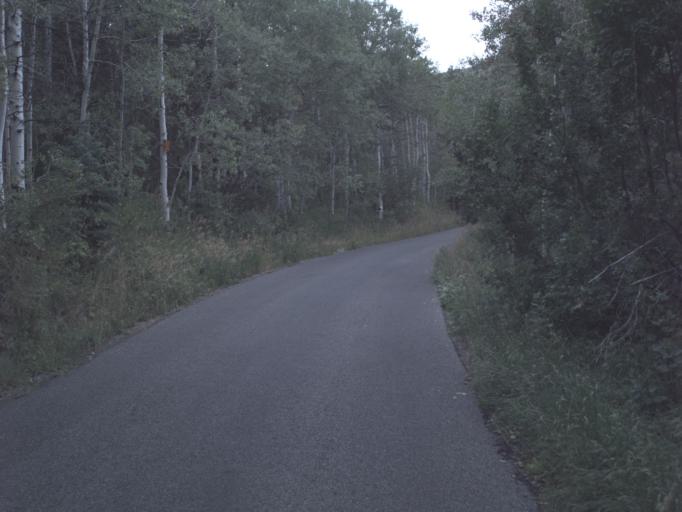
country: US
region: Utah
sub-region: Utah County
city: Lindon
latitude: 40.4137
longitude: -111.6024
